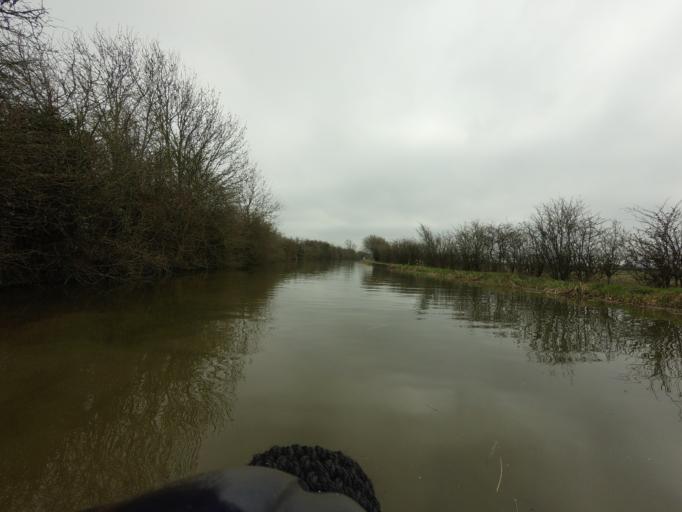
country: GB
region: England
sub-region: Buckinghamshire
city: Cheddington
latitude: 51.8788
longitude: -0.6581
